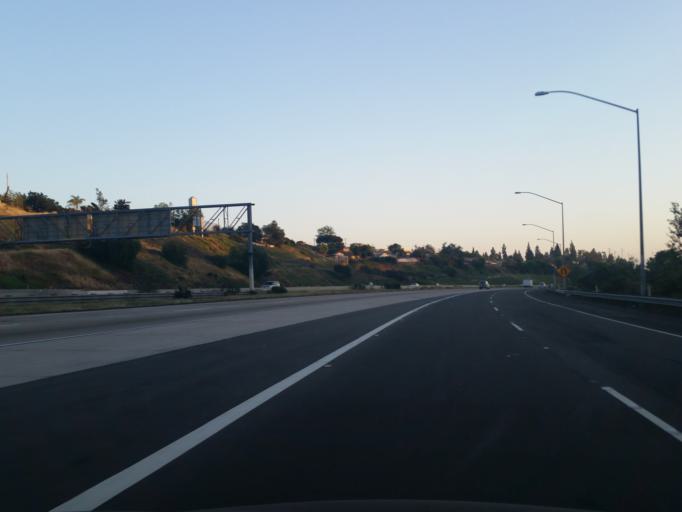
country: US
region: California
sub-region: San Diego County
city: San Diego
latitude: 32.7297
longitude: -117.1121
